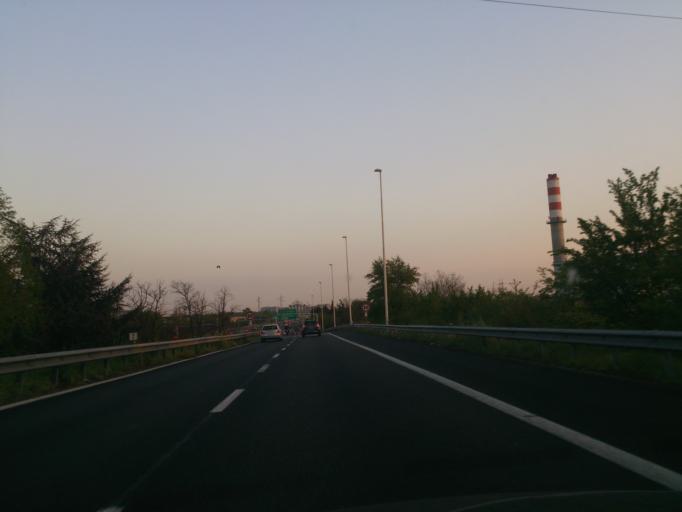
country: IT
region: Lombardy
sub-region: Citta metropolitana di Milano
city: Cologno Monzese
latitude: 45.5251
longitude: 9.2595
